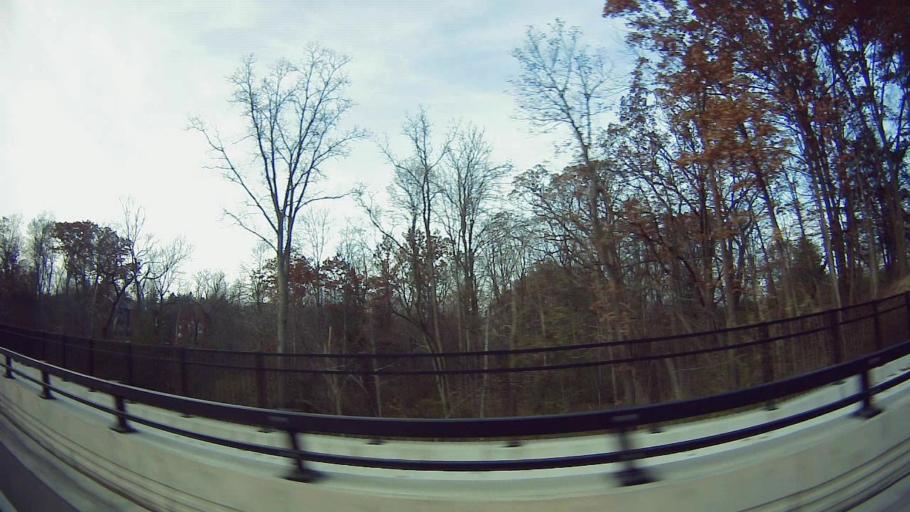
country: US
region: Michigan
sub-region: Oakland County
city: Bingham Farms
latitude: 42.5155
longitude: -83.2790
